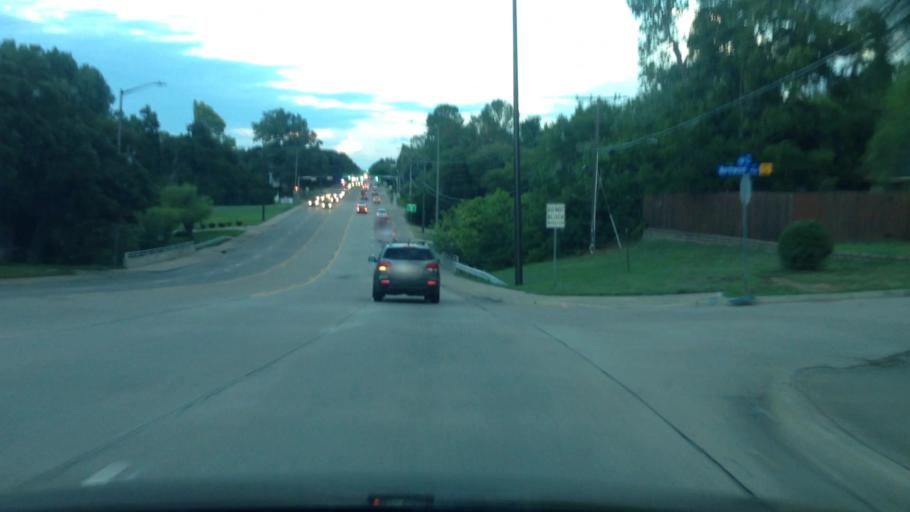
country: US
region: Texas
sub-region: Tarrant County
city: Arlington
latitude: 32.7589
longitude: -97.1318
